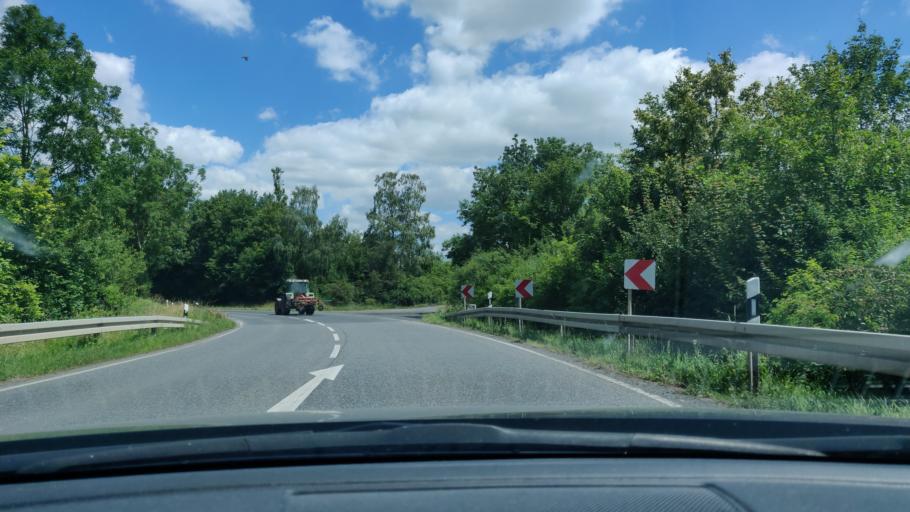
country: DE
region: Hesse
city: Fritzlar
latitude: 51.1404
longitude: 9.2871
